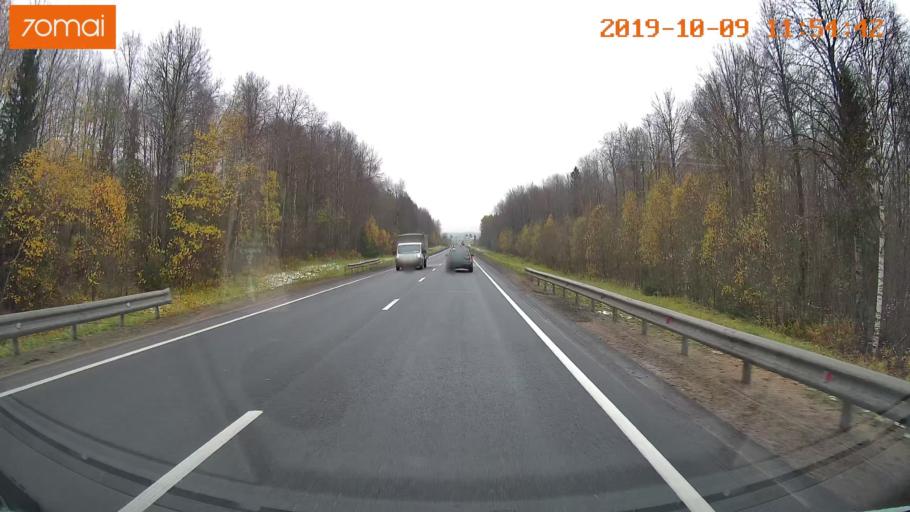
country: RU
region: Vologda
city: Gryazovets
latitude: 58.7560
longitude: 40.2826
